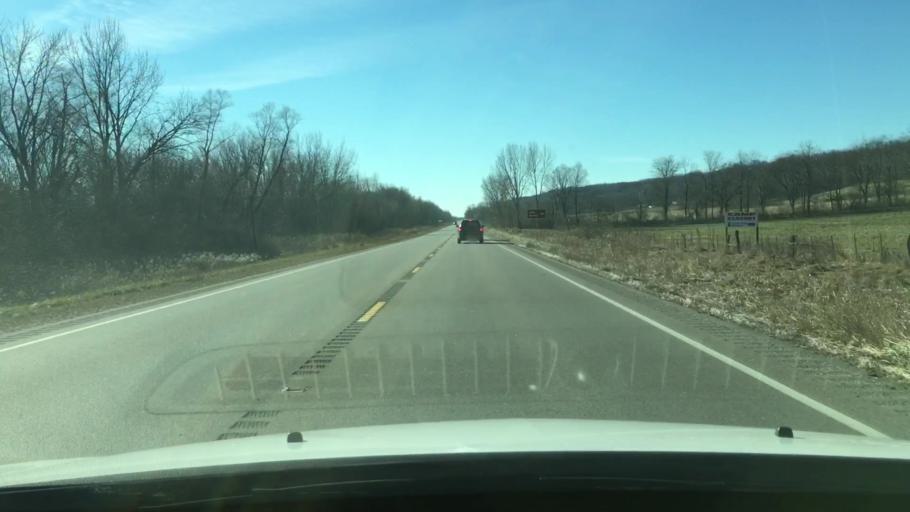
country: US
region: Illinois
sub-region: Peoria County
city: Glasford
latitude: 40.5452
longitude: -89.8587
